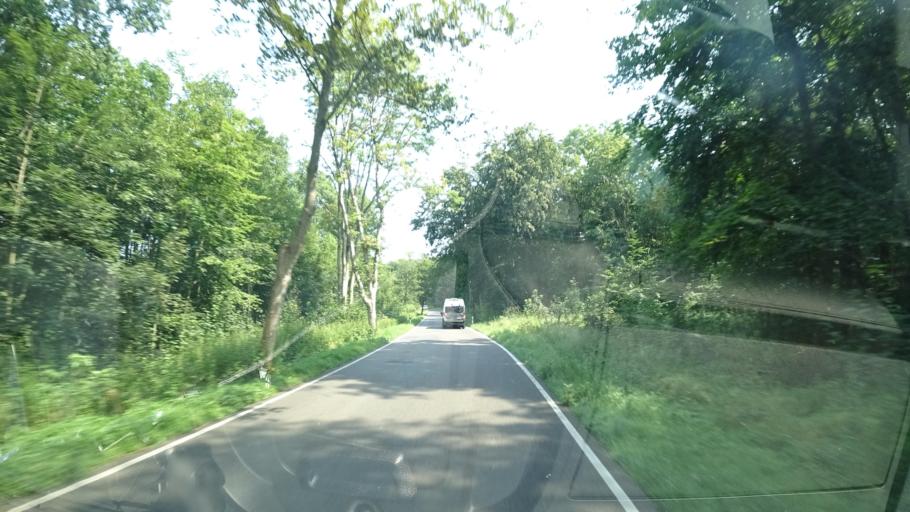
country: PL
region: West Pomeranian Voivodeship
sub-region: Swinoujscie
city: Swinoujscie
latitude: 53.8906
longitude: 14.1928
